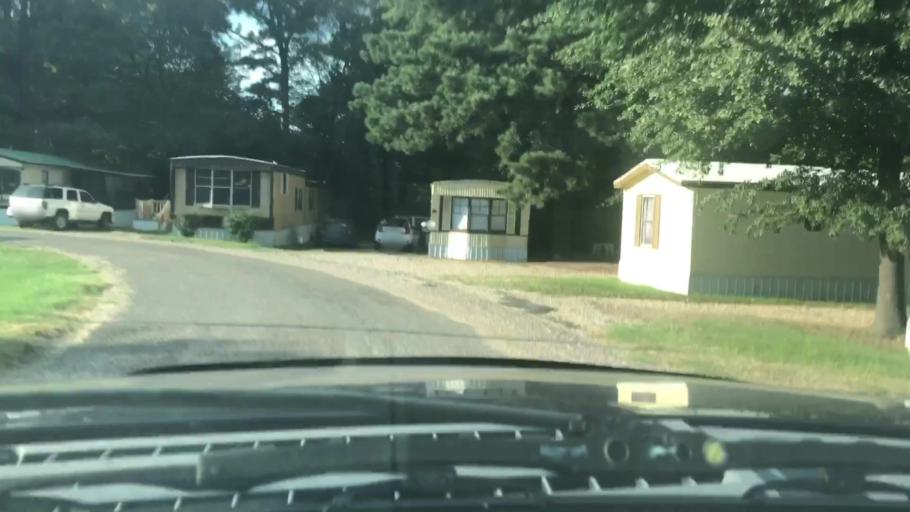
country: US
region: Texas
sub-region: Bowie County
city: Wake Village
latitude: 33.3775
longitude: -94.0945
